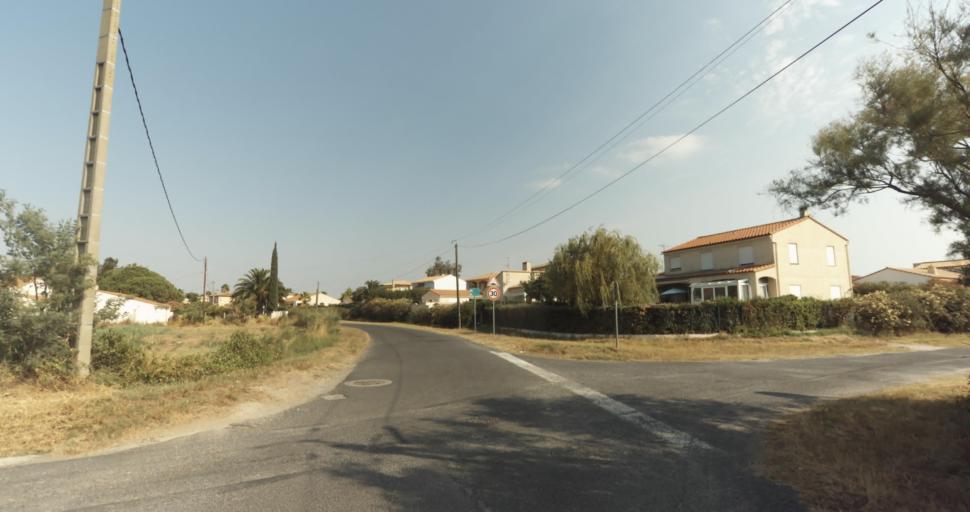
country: FR
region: Languedoc-Roussillon
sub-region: Departement des Pyrenees-Orientales
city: Latour-Bas-Elne
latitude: 42.6130
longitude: 3.0151
